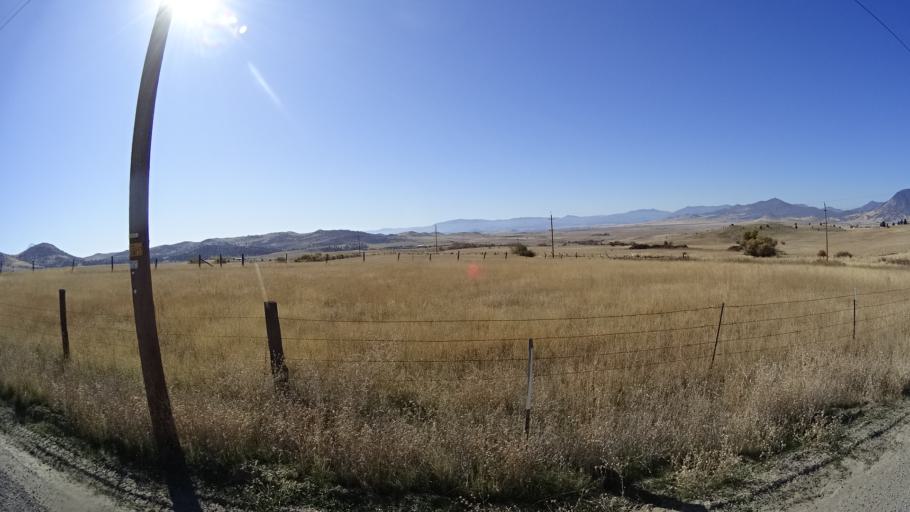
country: US
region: California
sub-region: Siskiyou County
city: Montague
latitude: 41.8304
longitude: -122.3702
